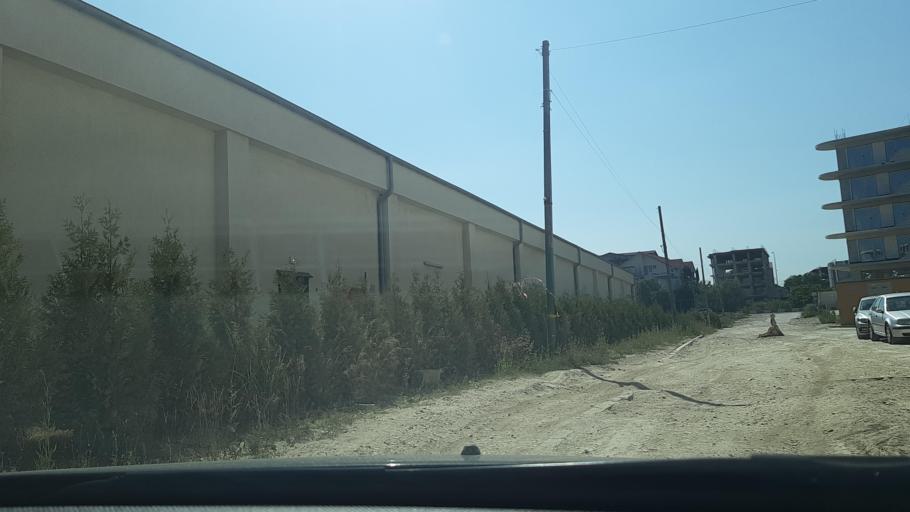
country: RO
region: Constanta
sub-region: Comuna Navodari
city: Navodari
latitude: 44.3073
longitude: 28.6232
